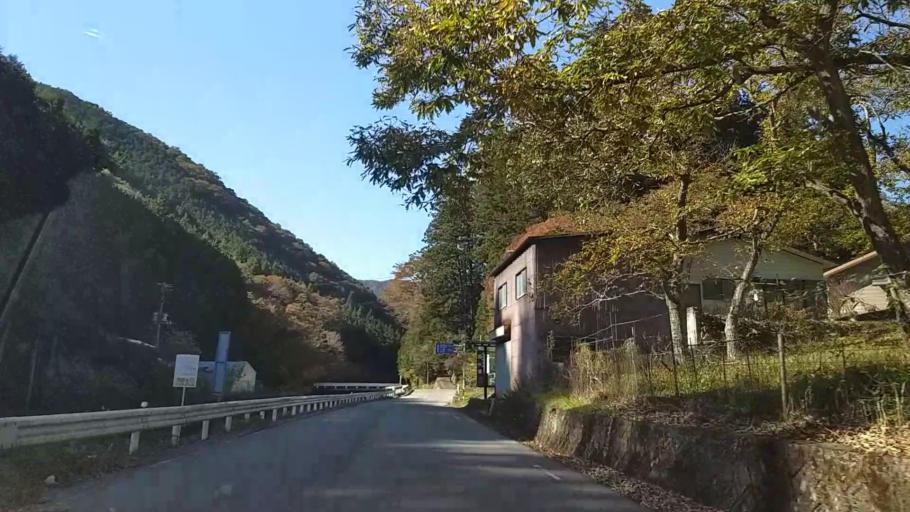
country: JP
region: Yamanashi
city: Otsuki
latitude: 35.7051
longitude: 139.0137
